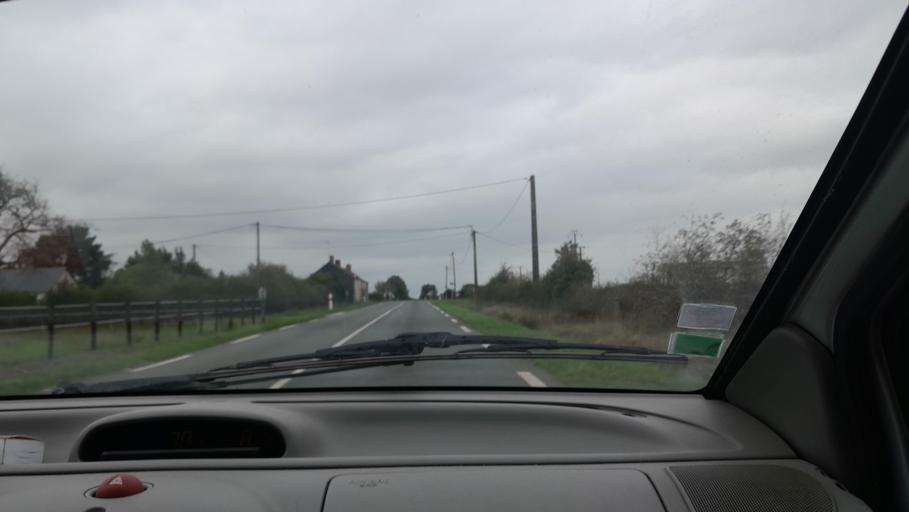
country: FR
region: Pays de la Loire
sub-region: Departement de la Loire-Atlantique
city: Saint-Mars-la-Jaille
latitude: 47.5705
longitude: -1.1885
